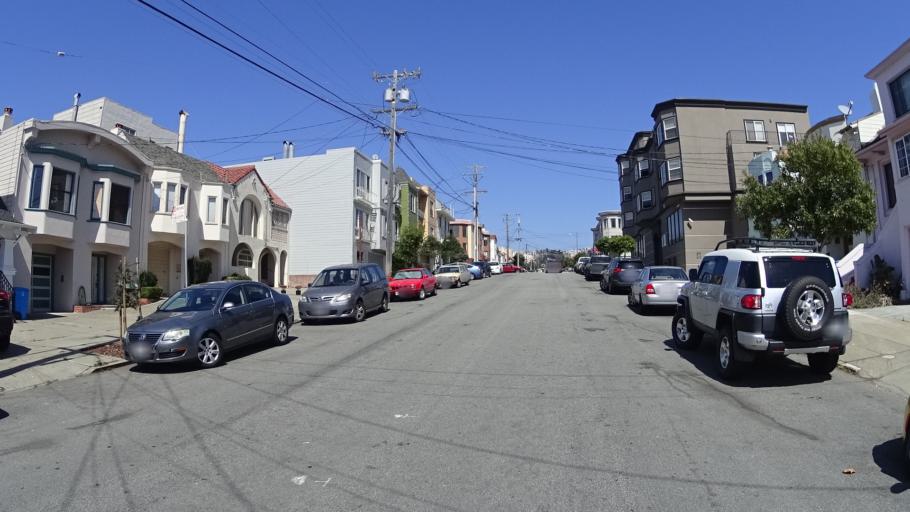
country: US
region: California
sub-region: San Mateo County
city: Daly City
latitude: 37.7420
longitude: -122.4831
